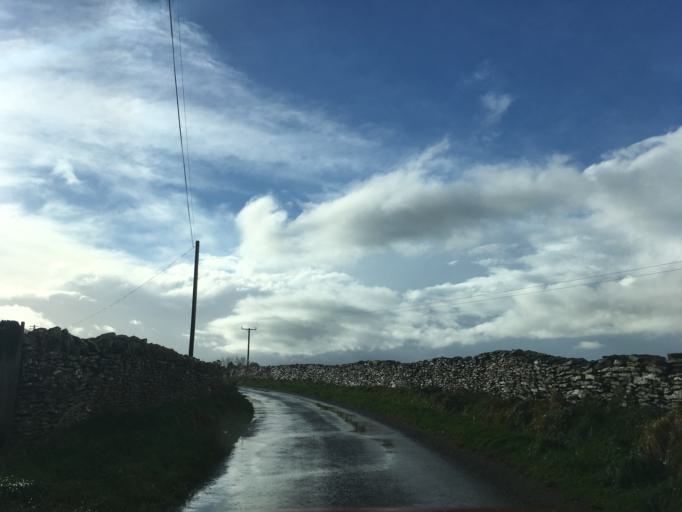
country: GB
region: England
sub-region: South Gloucestershire
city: Marshfield
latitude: 51.4695
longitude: -2.3291
